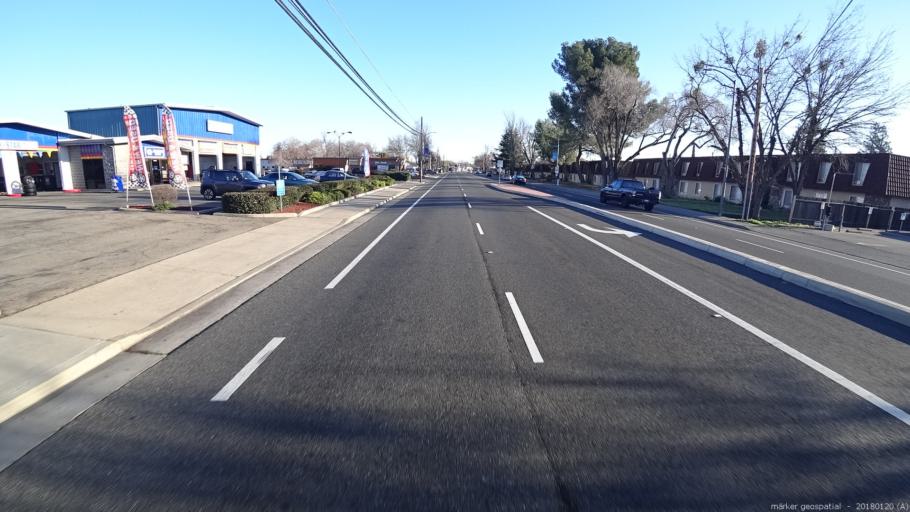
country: US
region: California
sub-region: Sacramento County
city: Rancho Cordova
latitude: 38.6114
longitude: -121.2909
